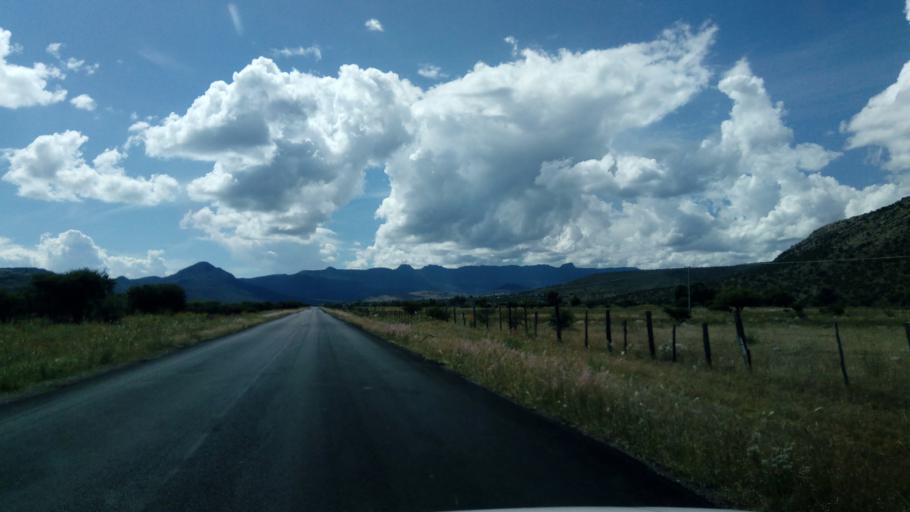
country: MX
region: Durango
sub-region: Durango
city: Jose Refugio Salcido
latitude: 23.8120
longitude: -104.4836
